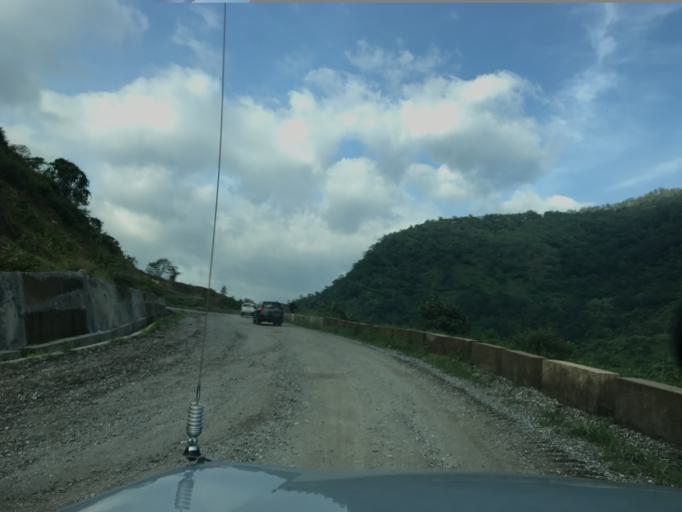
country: TL
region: Dili
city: Dili
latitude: -8.6359
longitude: 125.5108
